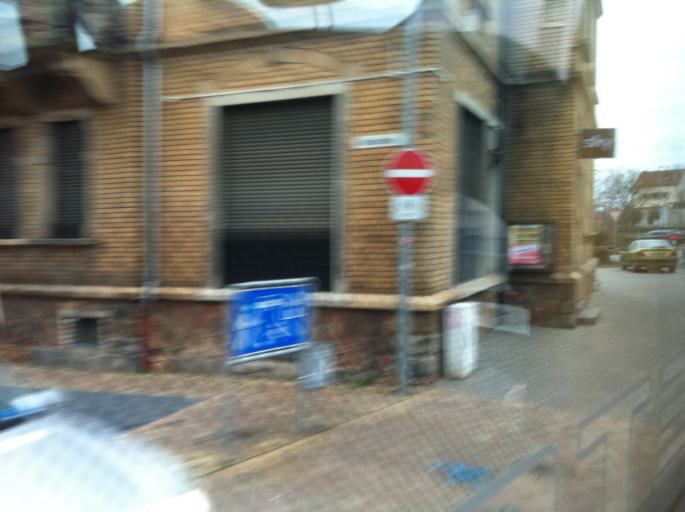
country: DE
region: Rheinland-Pfalz
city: Bad Kreuznach
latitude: 49.8433
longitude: 7.8632
